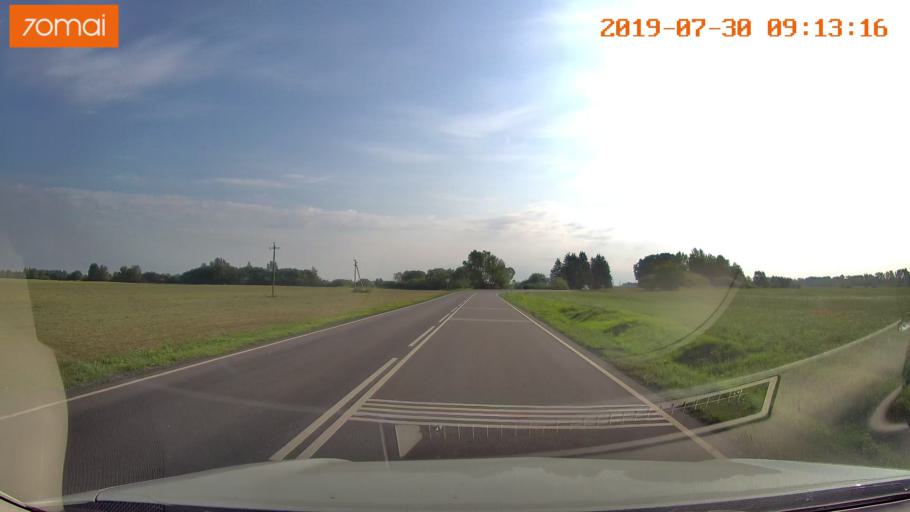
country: RU
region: Kaliningrad
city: Nesterov
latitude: 54.6239
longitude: 22.4935
